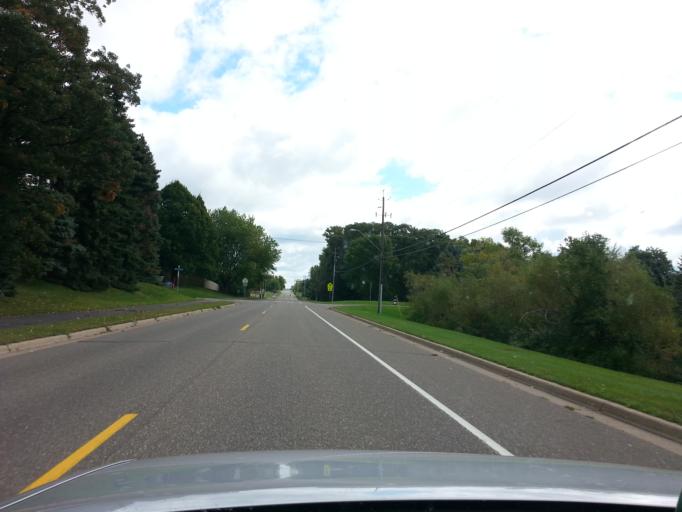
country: US
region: Minnesota
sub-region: Washington County
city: Oakdale
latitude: 44.9705
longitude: -92.9510
